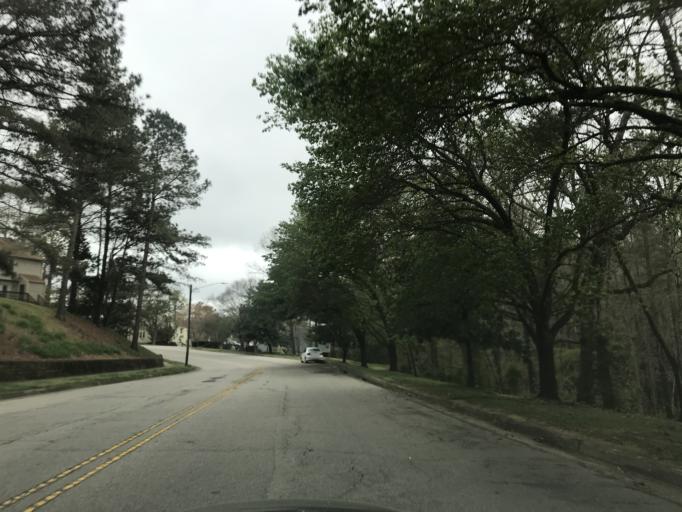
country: US
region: North Carolina
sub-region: Wake County
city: West Raleigh
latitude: 35.8736
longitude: -78.6478
